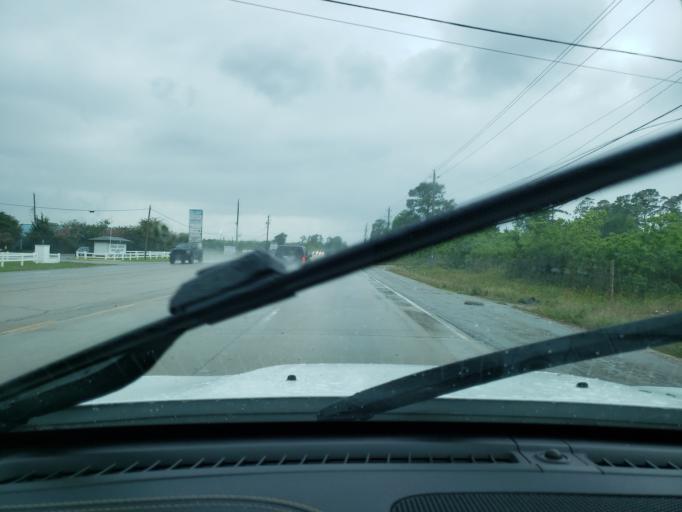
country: US
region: Texas
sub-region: Chambers County
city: Mont Belvieu
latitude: 29.7890
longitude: -94.9110
